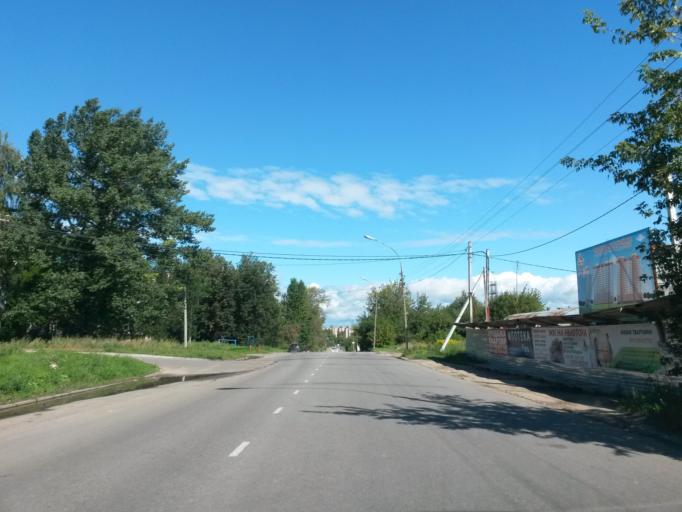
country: RU
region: Jaroslavl
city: Yaroslavl
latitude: 57.5808
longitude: 39.8657
